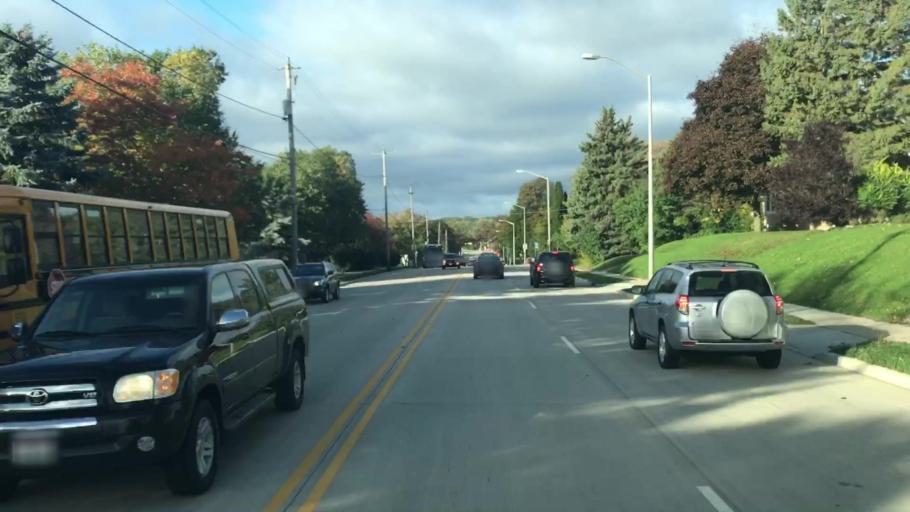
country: US
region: Wisconsin
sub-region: Waukesha County
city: Waukesha
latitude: 43.0237
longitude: -88.2115
